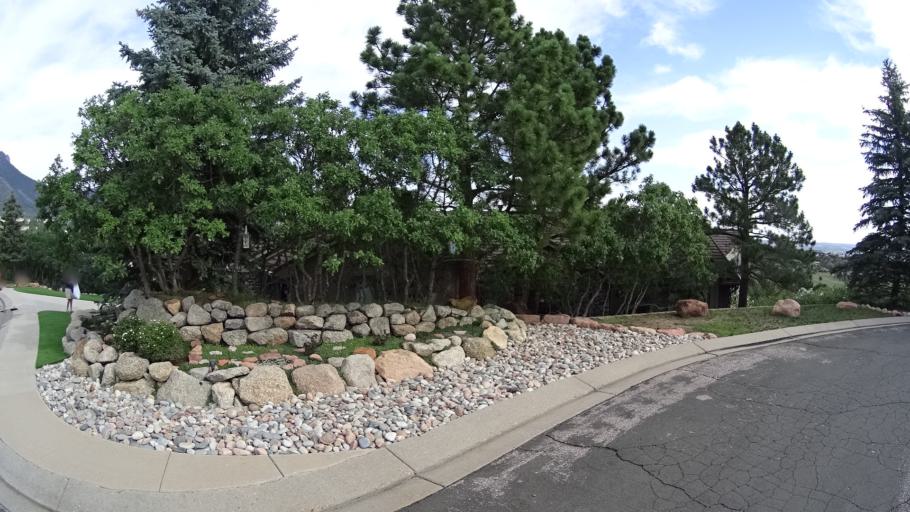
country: US
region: Colorado
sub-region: El Paso County
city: Air Force Academy
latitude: 38.9483
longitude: -104.8610
